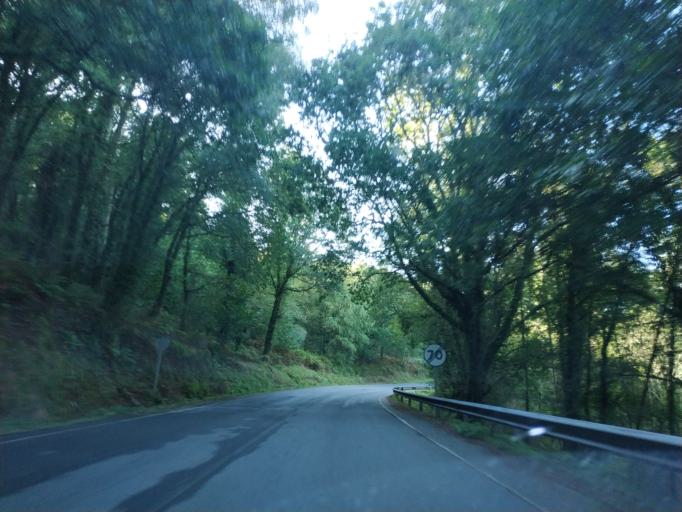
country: ES
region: Galicia
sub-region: Provincia da Coruna
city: Negreira
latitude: 42.9066
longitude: -8.7461
